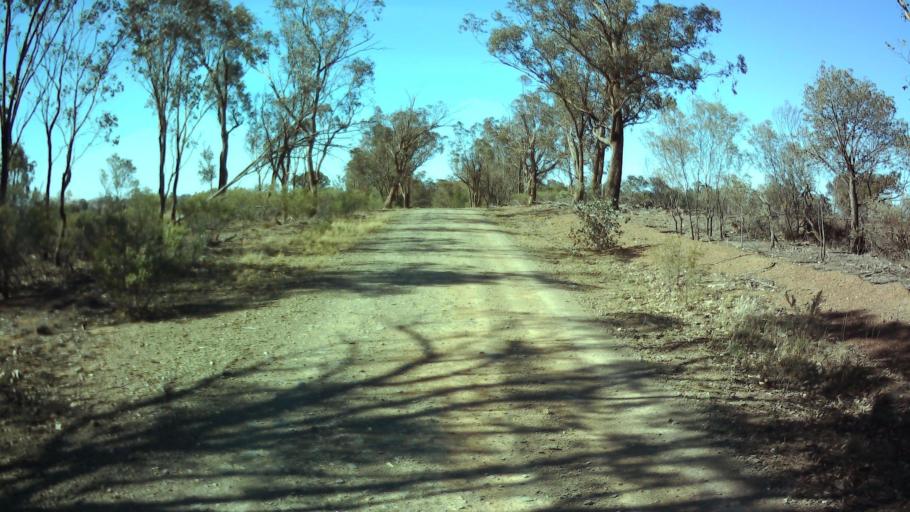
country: AU
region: New South Wales
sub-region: Weddin
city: Grenfell
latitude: -33.7477
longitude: 147.8306
